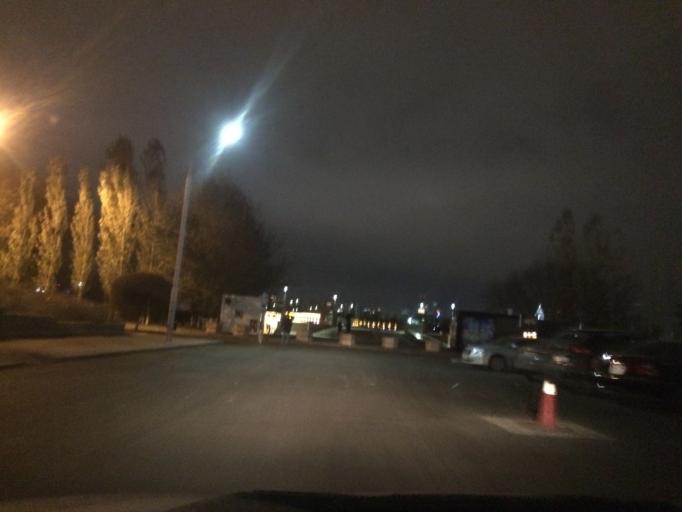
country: KZ
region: Astana Qalasy
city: Astana
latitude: 51.1615
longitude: 71.4182
